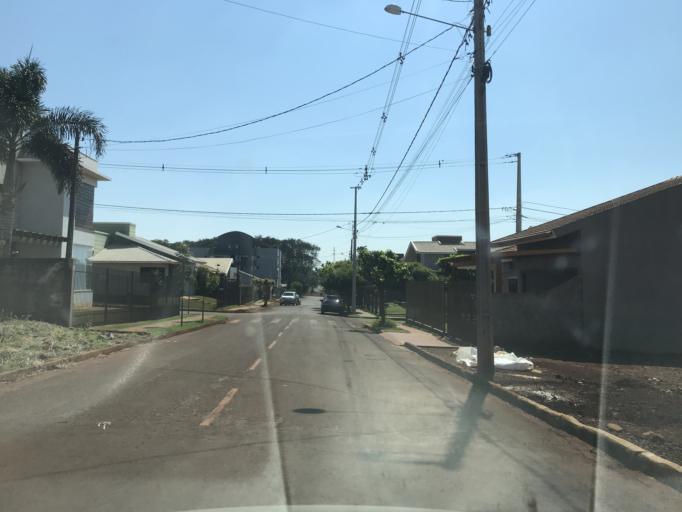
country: BR
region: Parana
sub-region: Palotina
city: Palotina
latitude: -24.2930
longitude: -53.8344
